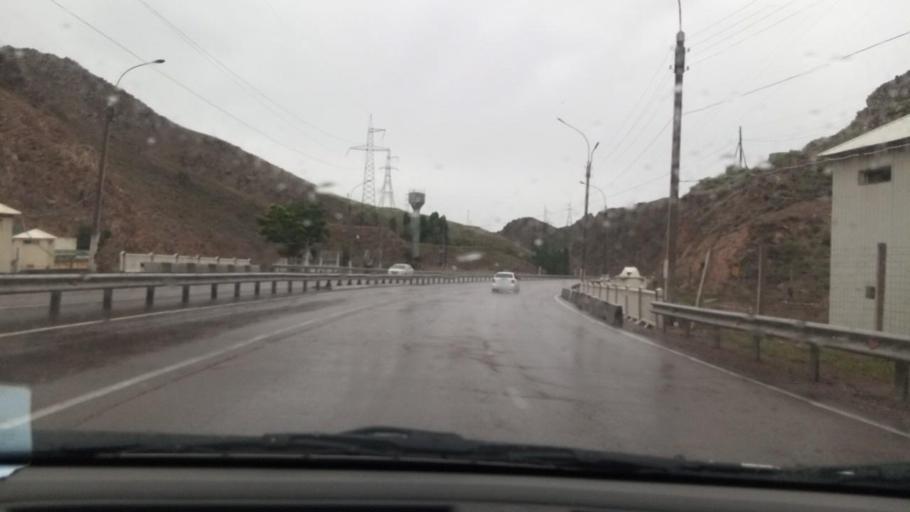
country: TJ
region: Viloyati Sughd
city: Shaydon
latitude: 40.9605
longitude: 70.6653
